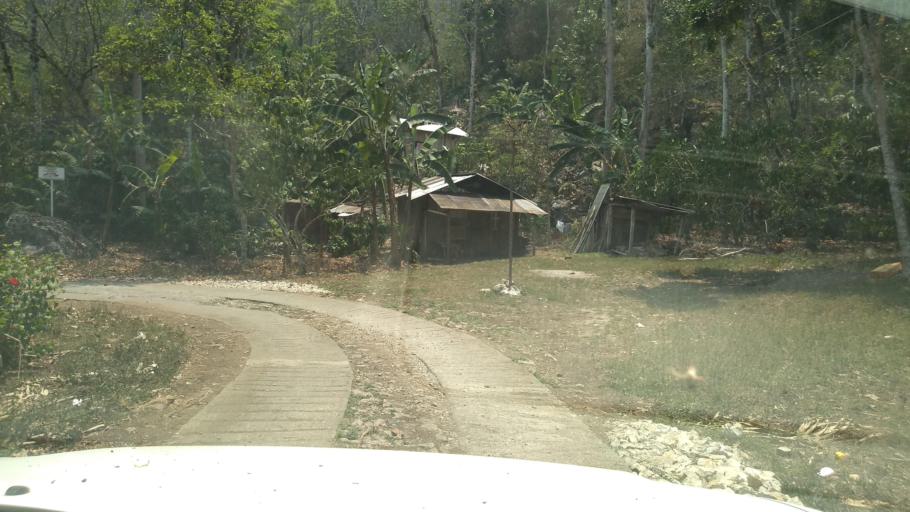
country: MX
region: Veracruz
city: Cosolapa
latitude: 18.6009
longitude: -96.7268
